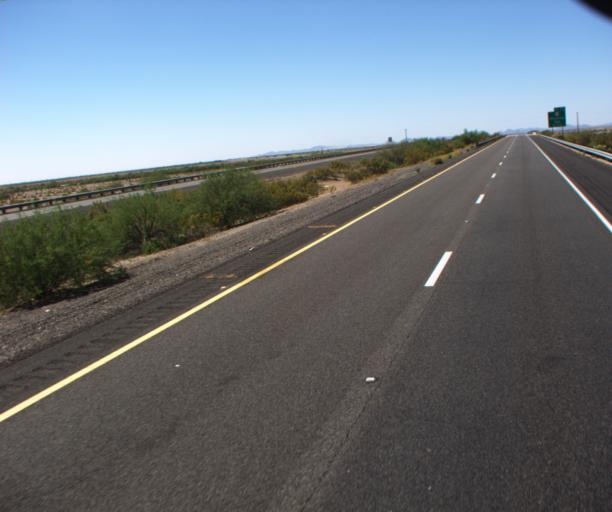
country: US
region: Arizona
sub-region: Maricopa County
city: Gila Bend
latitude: 32.9363
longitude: -112.7194
